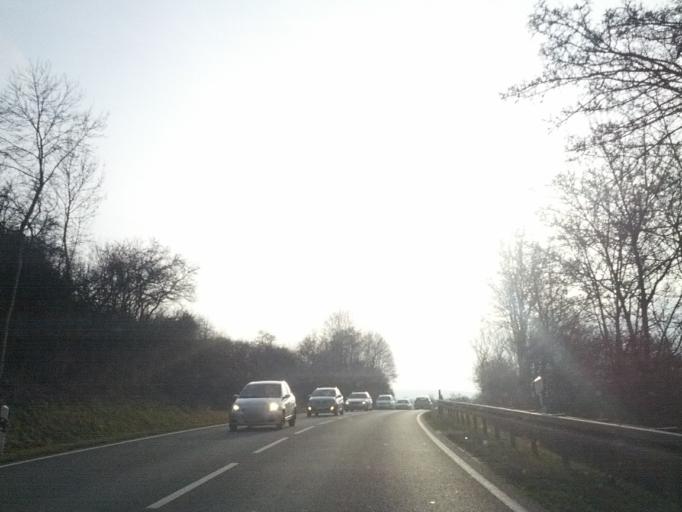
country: DE
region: Thuringia
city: Walldorf
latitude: 50.6129
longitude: 10.4020
